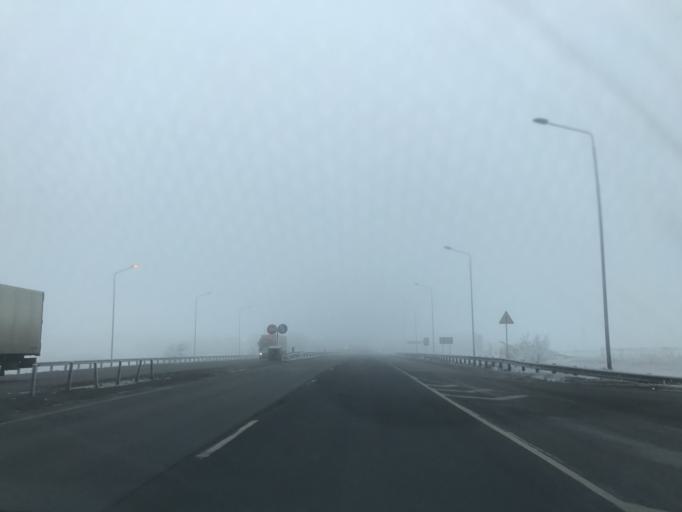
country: RU
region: Rostov
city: Likhoy
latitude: 48.1661
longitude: 40.2631
